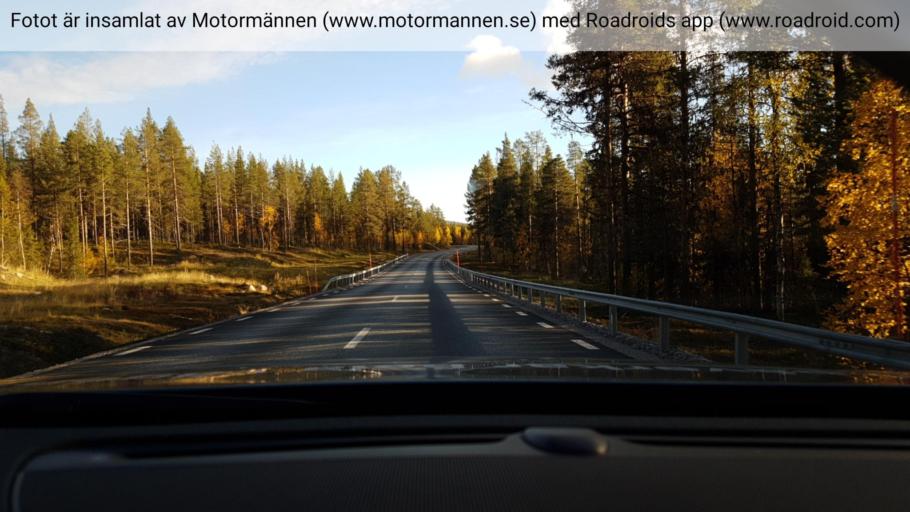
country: SE
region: Norrbotten
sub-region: Jokkmokks Kommun
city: Jokkmokk
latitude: 66.9232
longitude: 19.8270
